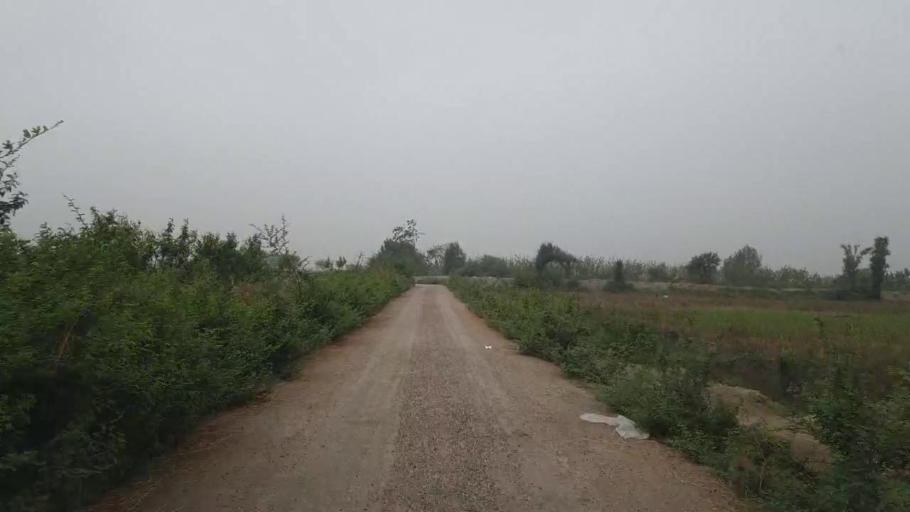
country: PK
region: Sindh
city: Badin
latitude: 24.5708
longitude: 68.6586
